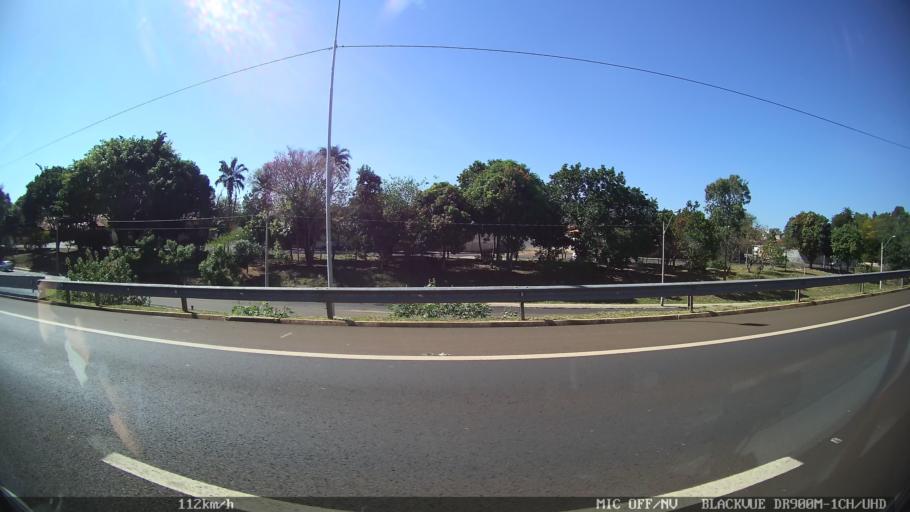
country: BR
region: Sao Paulo
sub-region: Franca
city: Franca
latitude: -20.4882
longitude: -47.4085
